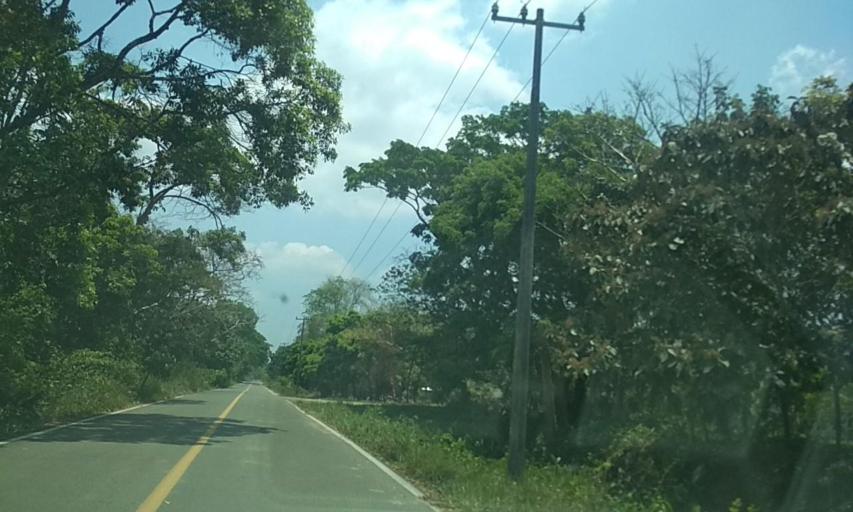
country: MX
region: Tabasco
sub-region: Huimanguillo
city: Francisco Rueda
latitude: 17.7503
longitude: -94.0445
